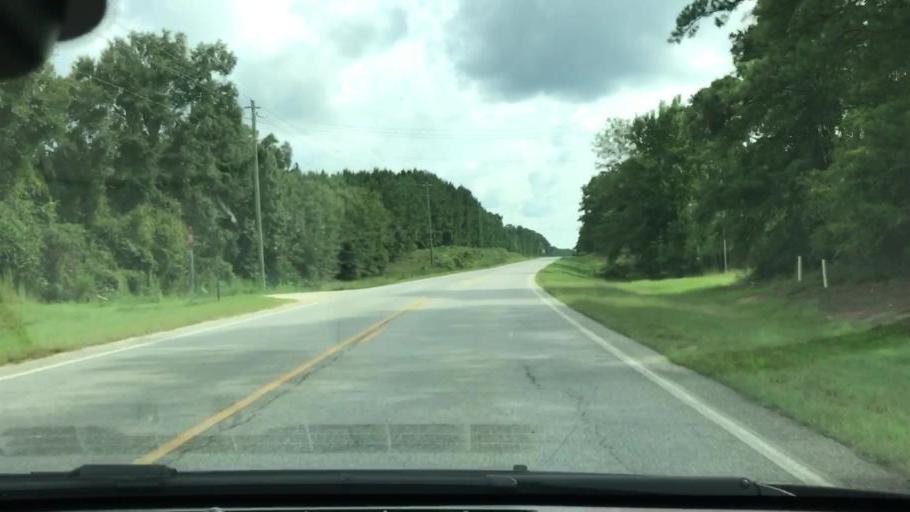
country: US
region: Georgia
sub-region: Clay County
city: Fort Gaines
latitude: 31.6447
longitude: -85.0441
